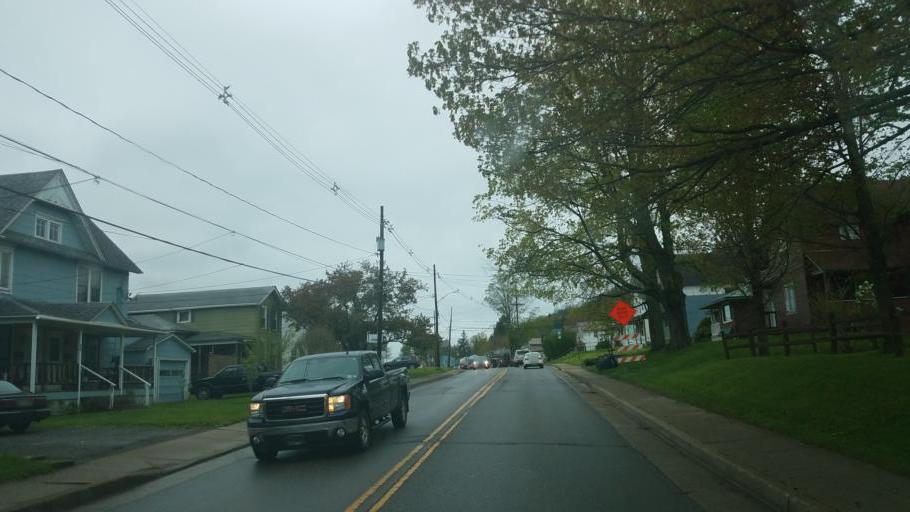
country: US
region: Pennsylvania
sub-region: McKean County
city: Port Allegany
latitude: 41.8184
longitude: -78.2858
